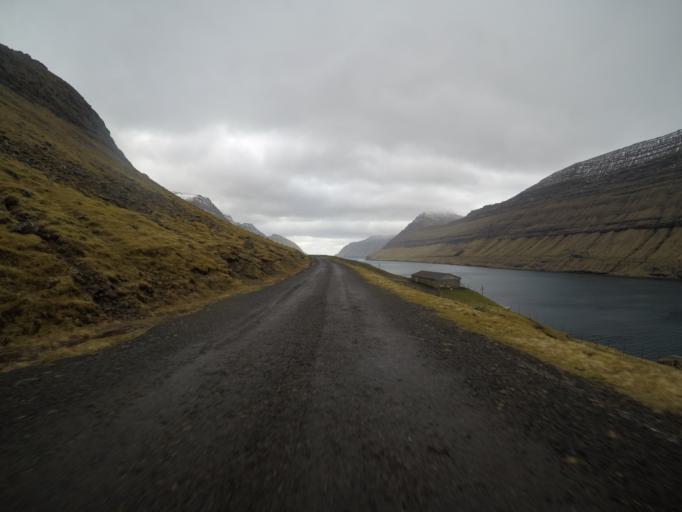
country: FO
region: Nordoyar
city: Klaksvik
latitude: 62.3049
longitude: -6.5389
